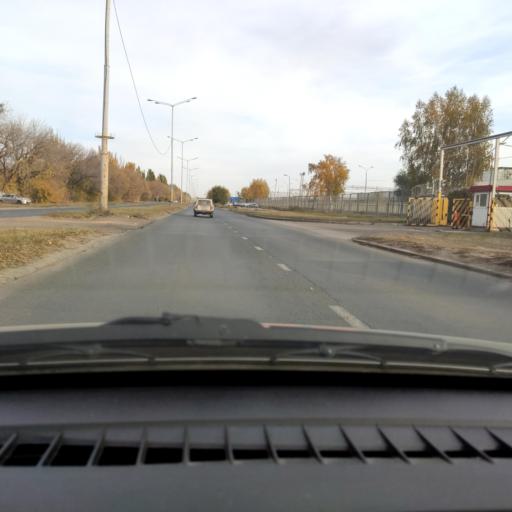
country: RU
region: Samara
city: Tol'yatti
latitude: 53.5693
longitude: 49.2595
